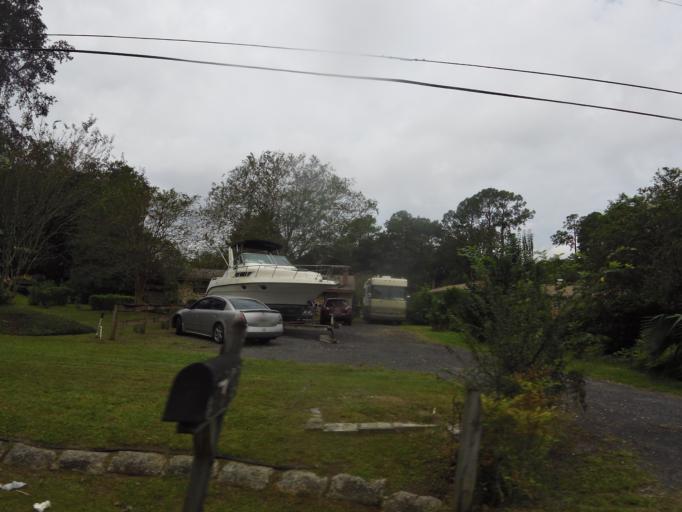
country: US
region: Florida
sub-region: Clay County
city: Bellair-Meadowbrook Terrace
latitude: 30.2496
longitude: -81.7307
